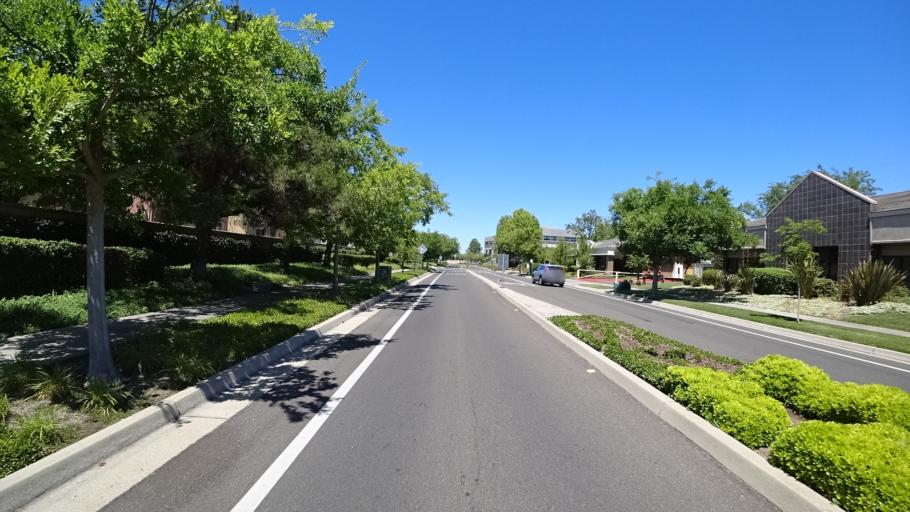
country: US
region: California
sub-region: Yolo County
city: West Sacramento
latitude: 38.6521
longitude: -121.5332
